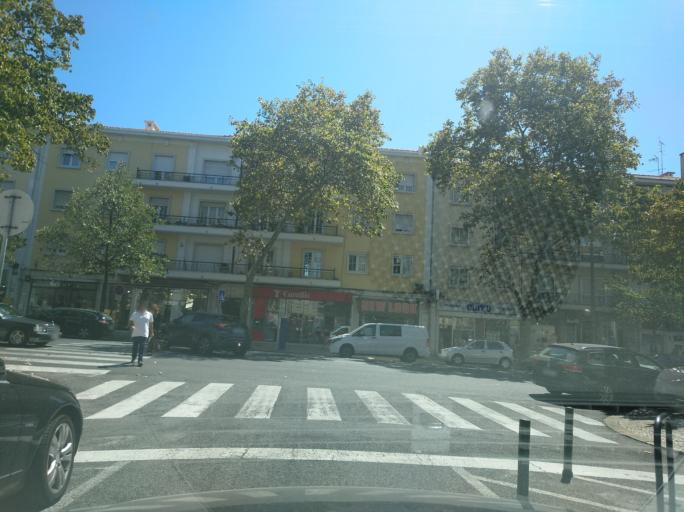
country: PT
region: Lisbon
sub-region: Lisbon
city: Lisbon
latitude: 38.7541
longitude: -9.1415
